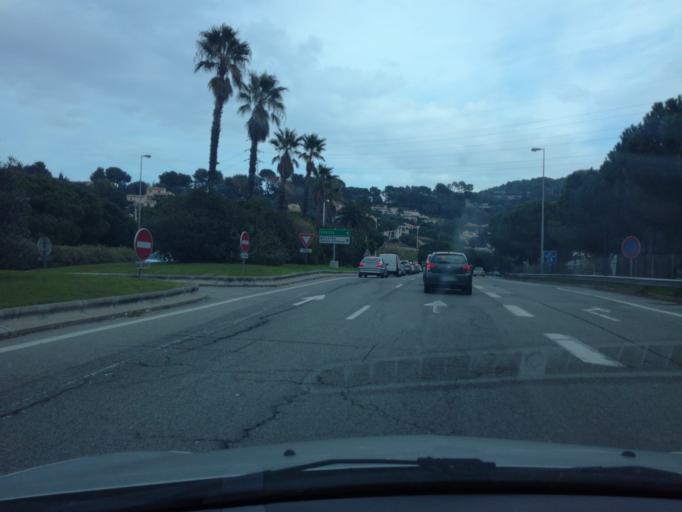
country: FR
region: Provence-Alpes-Cote d'Azur
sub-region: Departement des Alpes-Maritimes
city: Mougins
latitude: 43.5850
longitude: 7.0051
